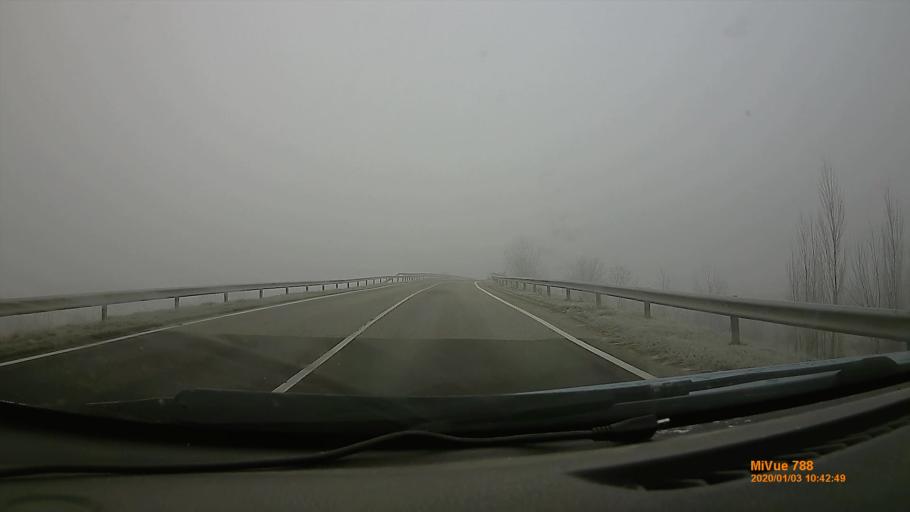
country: HU
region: Tolna
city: Bataszek
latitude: 46.2082
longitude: 18.7047
